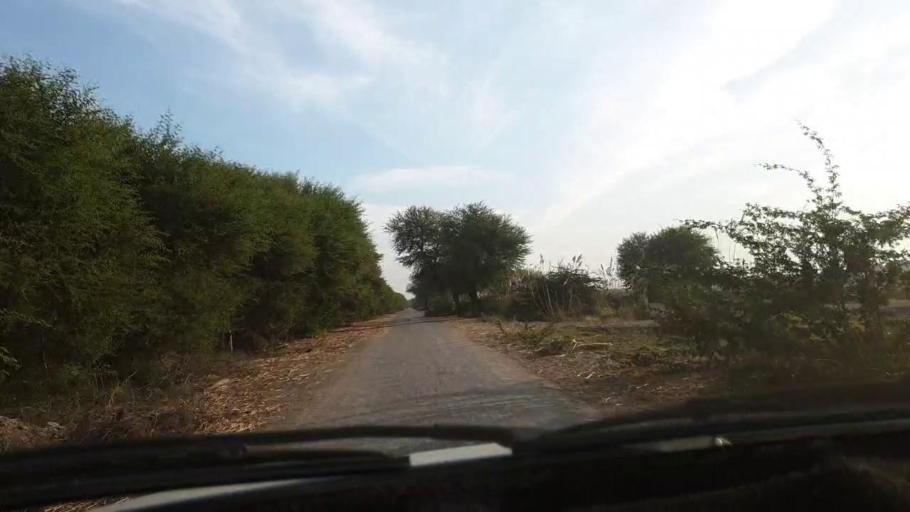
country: PK
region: Sindh
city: Bulri
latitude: 25.0191
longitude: 68.2889
